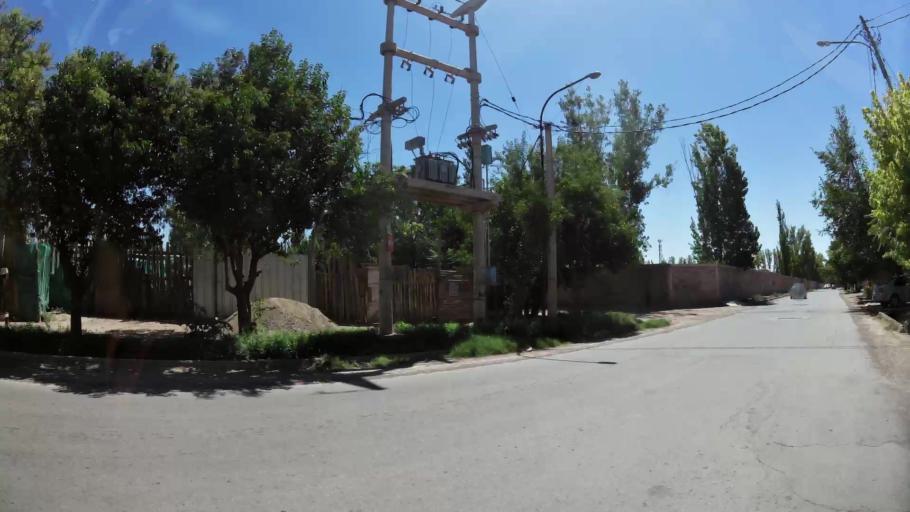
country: AR
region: Mendoza
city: Villa Nueva
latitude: -32.8742
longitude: -68.7860
